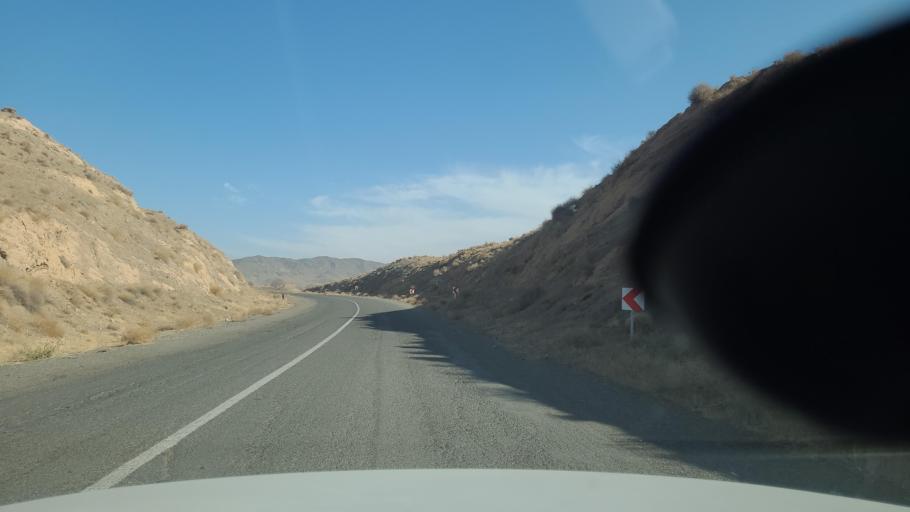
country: IR
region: Razavi Khorasan
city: Fariman
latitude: 35.5931
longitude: 59.6904
